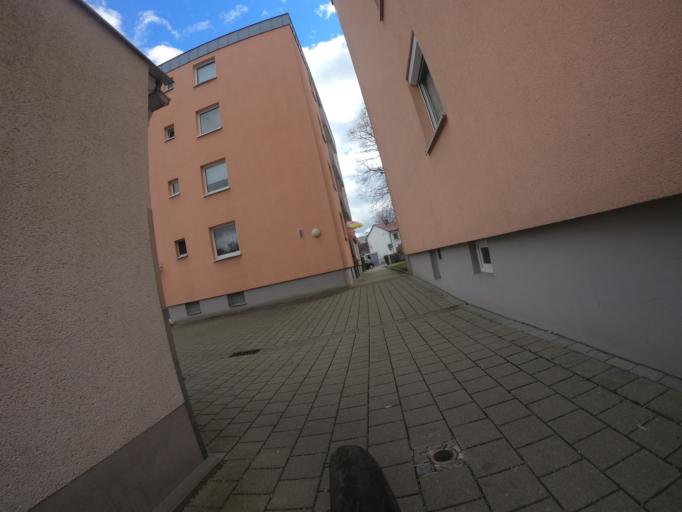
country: DE
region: Bavaria
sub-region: Upper Bavaria
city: Fuerstenfeldbruck
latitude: 48.1711
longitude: 11.2306
